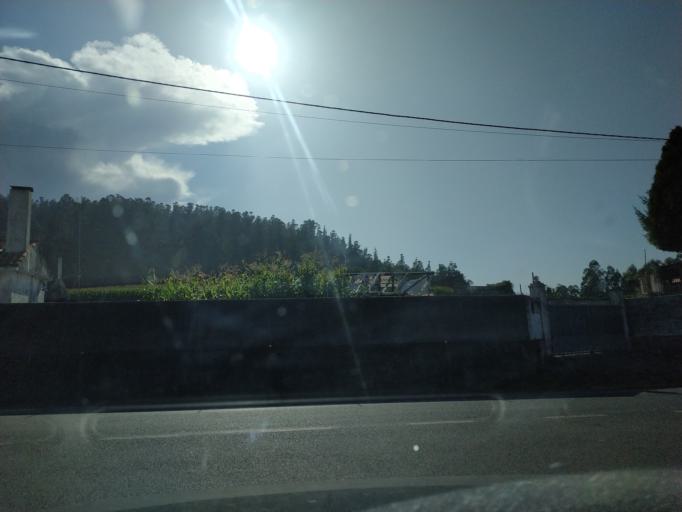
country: ES
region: Galicia
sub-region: Provincia da Coruna
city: Cerceda
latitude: 43.2285
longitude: -8.4945
